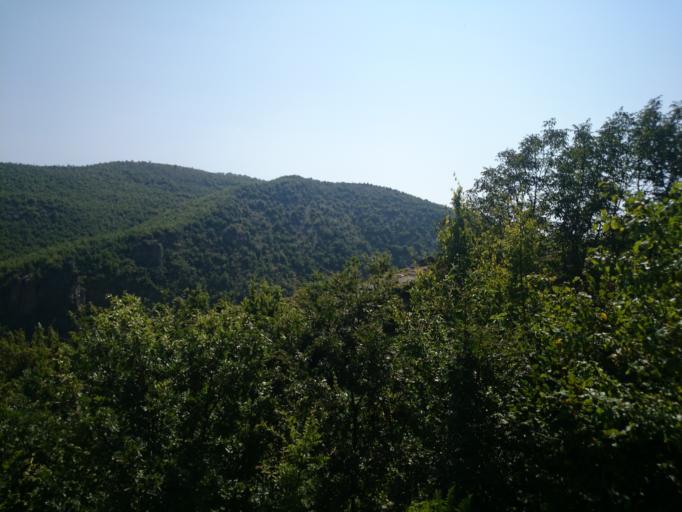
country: AL
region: Diber
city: Peshkopi
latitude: 41.6332
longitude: 20.4098
